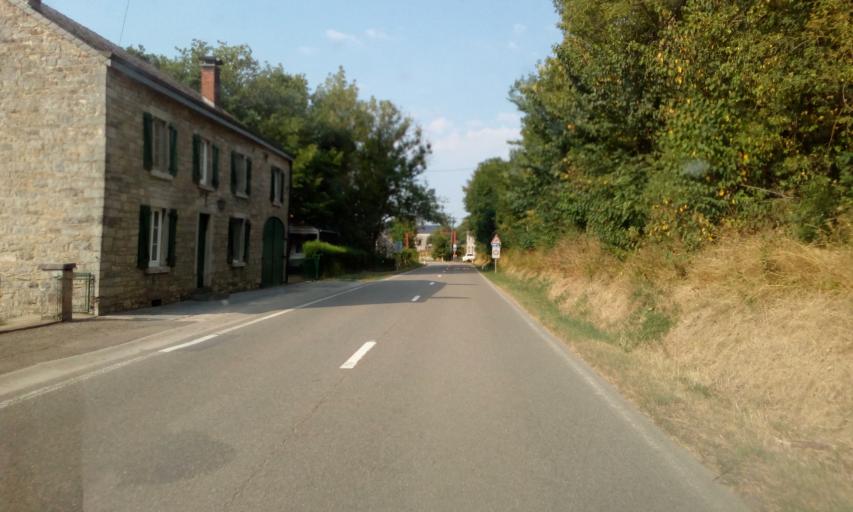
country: BE
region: Wallonia
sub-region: Province du Luxembourg
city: Tellin
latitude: 50.1183
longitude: 5.2469
